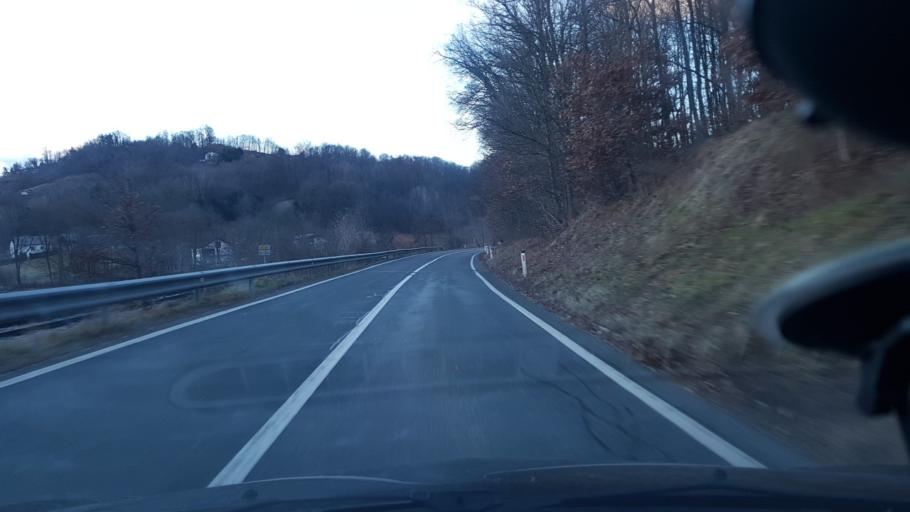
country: HR
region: Krapinsko-Zagorska
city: Pregrada
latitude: 46.2106
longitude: 15.7524
